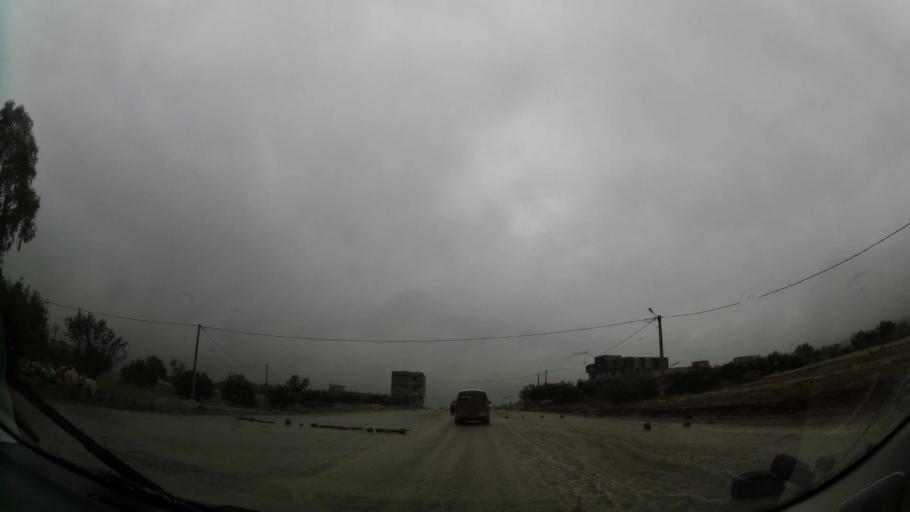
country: MA
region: Oriental
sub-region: Nador
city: Midar
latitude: 34.8711
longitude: -3.7258
